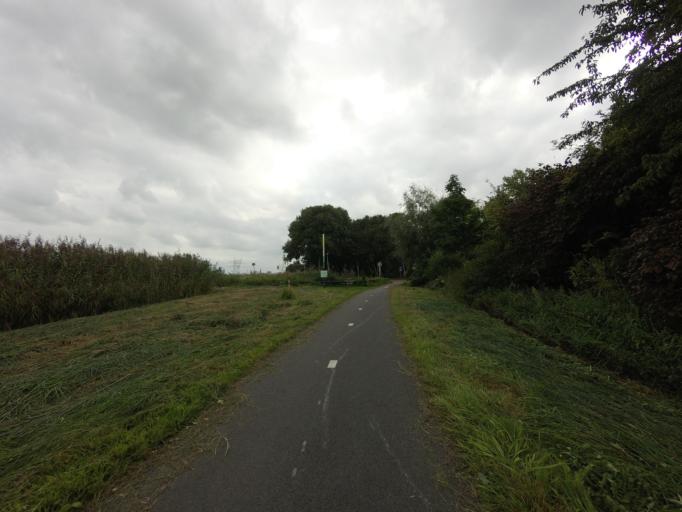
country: NL
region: North Holland
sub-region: Gemeente Diemen
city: Diemen
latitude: 52.3841
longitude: 4.9759
